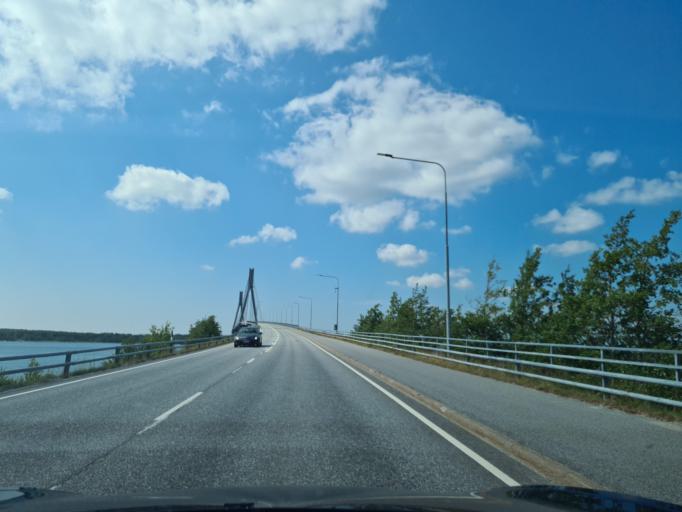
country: FI
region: Ostrobothnia
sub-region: Vaasa
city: Replot
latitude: 63.2065
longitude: 21.4866
